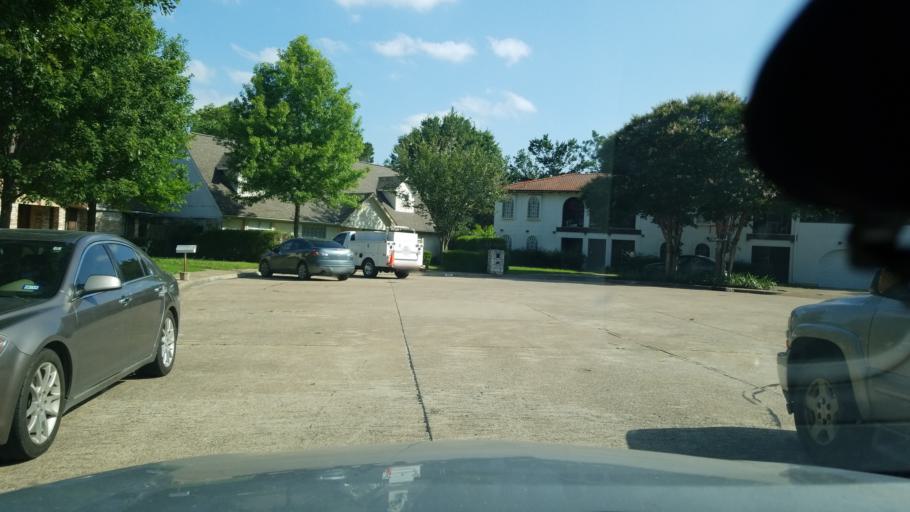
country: US
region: Texas
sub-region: Dallas County
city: Irving
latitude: 32.8221
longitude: -96.9725
